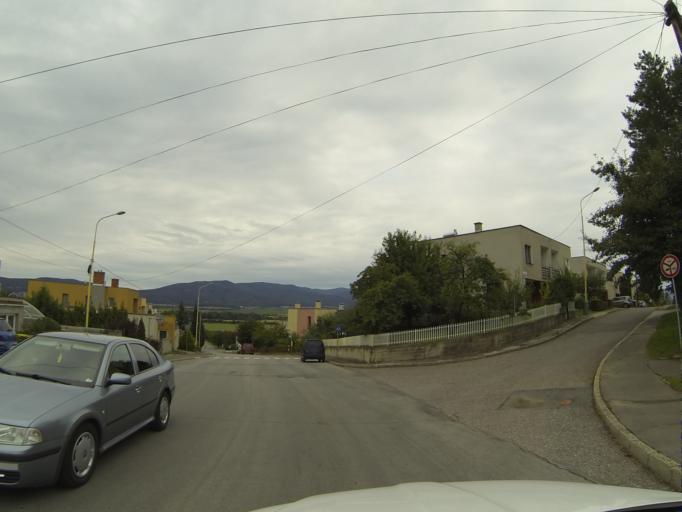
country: SK
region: Nitriansky
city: Prievidza
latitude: 48.7864
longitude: 18.6410
